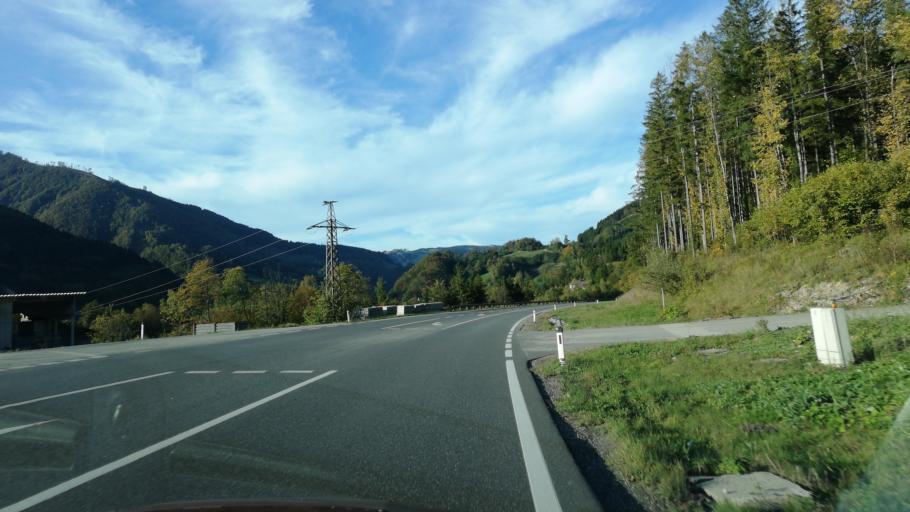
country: AT
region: Upper Austria
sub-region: Politischer Bezirk Steyr-Land
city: Weyer
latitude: 47.8020
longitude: 14.6460
